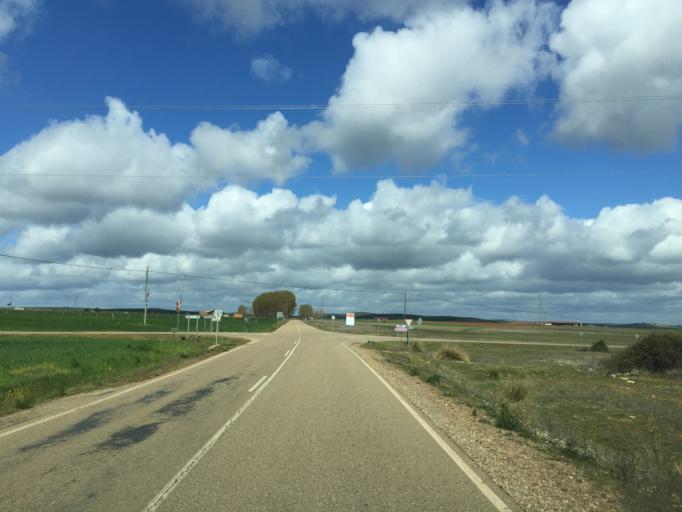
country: ES
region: Castille and Leon
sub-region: Provincia de Zamora
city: Palacios del Pan
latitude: 41.5770
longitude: -5.9240
